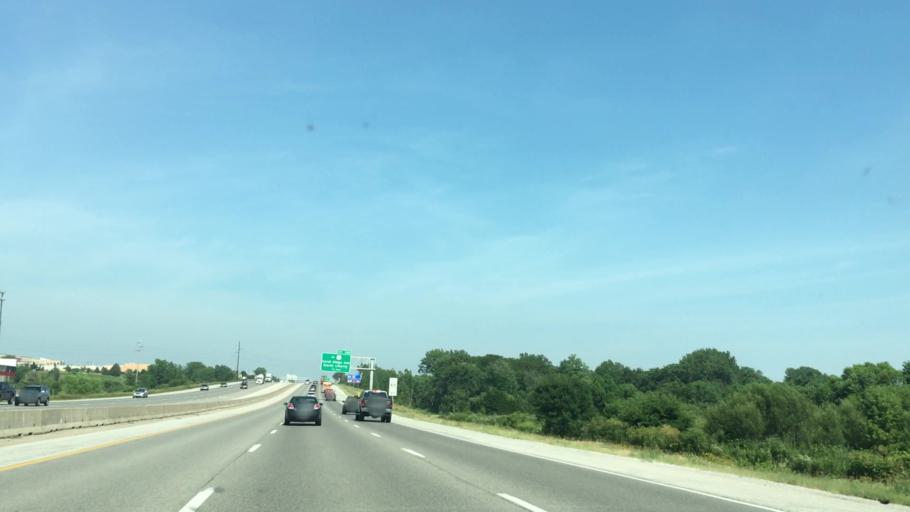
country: US
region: Iowa
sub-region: Johnson County
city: Tiffin
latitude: 41.6943
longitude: -91.6276
